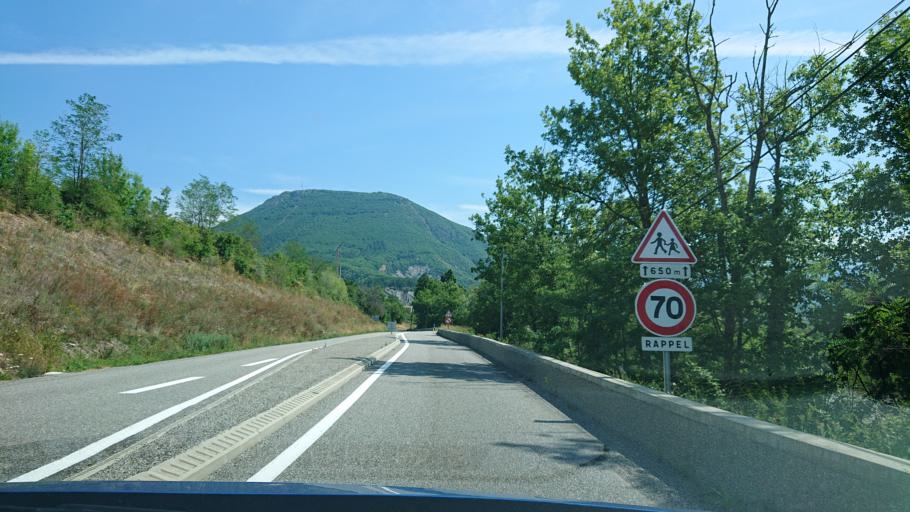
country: FR
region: Provence-Alpes-Cote d'Azur
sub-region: Departement des Alpes-de-Haute-Provence
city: Sisteron
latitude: 44.2580
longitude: 5.9656
